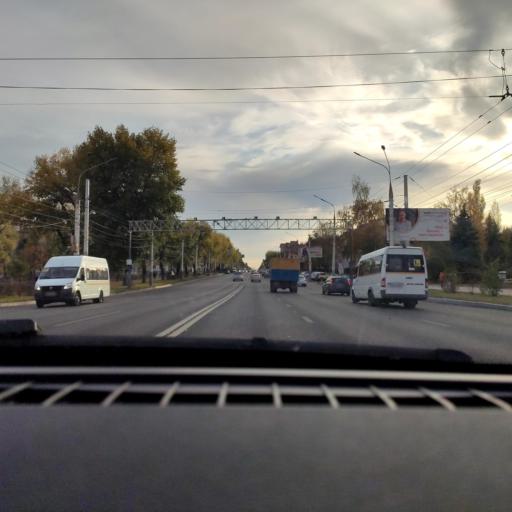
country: RU
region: Voronezj
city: Voronezh
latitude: 51.6592
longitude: 39.2457
